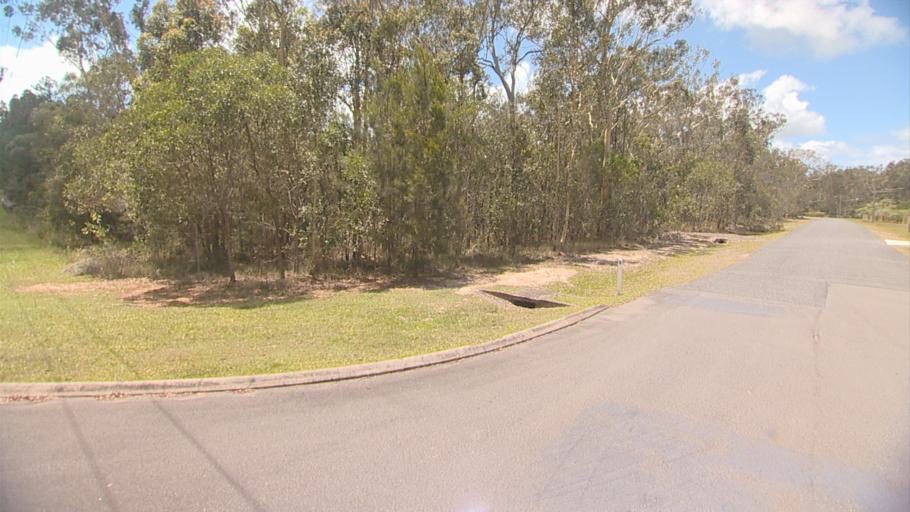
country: AU
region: Queensland
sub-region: Gold Coast
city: Yatala
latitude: -27.6827
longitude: 153.2747
